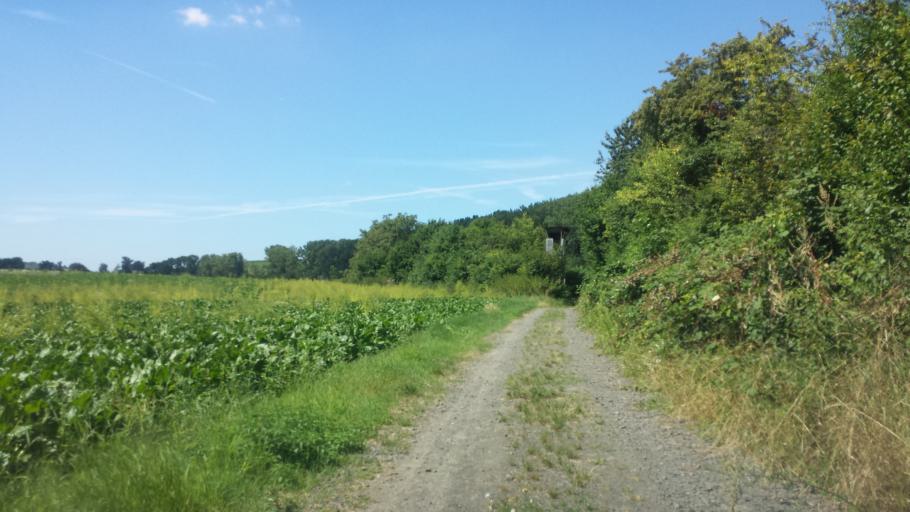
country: DE
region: Rheinland-Pfalz
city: Monsheim
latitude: 49.6362
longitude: 8.1975
